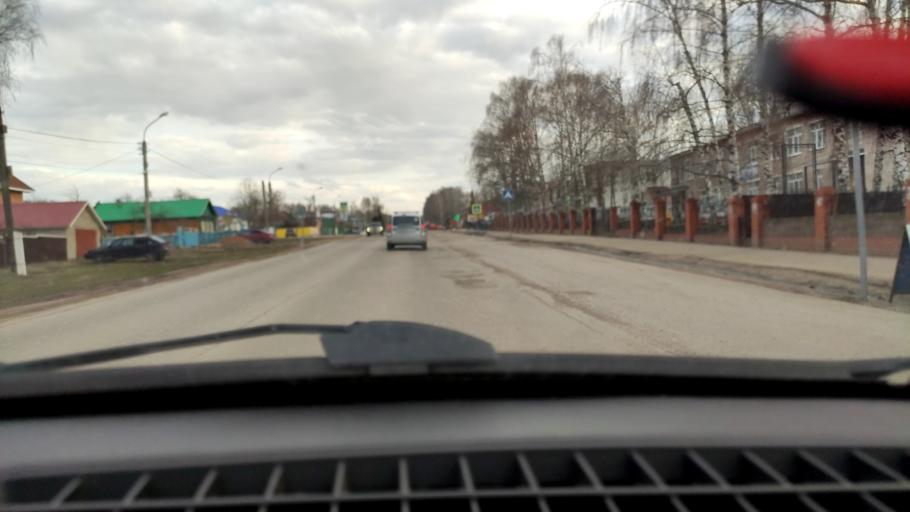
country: RU
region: Bashkortostan
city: Tolbazy
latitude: 54.0194
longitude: 55.8864
